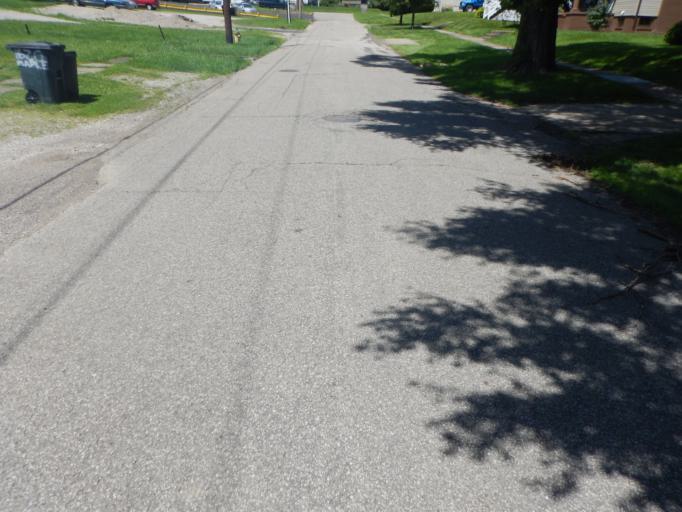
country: US
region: Ohio
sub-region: Muskingum County
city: Zanesville
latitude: 39.9586
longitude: -82.0096
